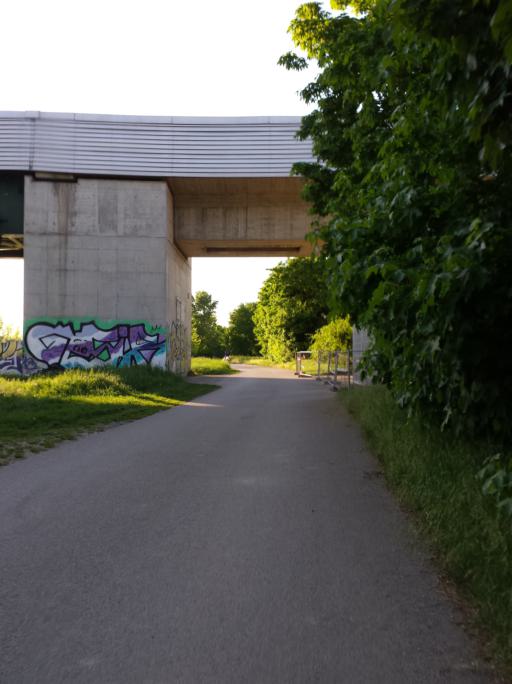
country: AT
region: Vienna
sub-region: Wien Stadt
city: Vienna
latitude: 48.2087
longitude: 16.4361
